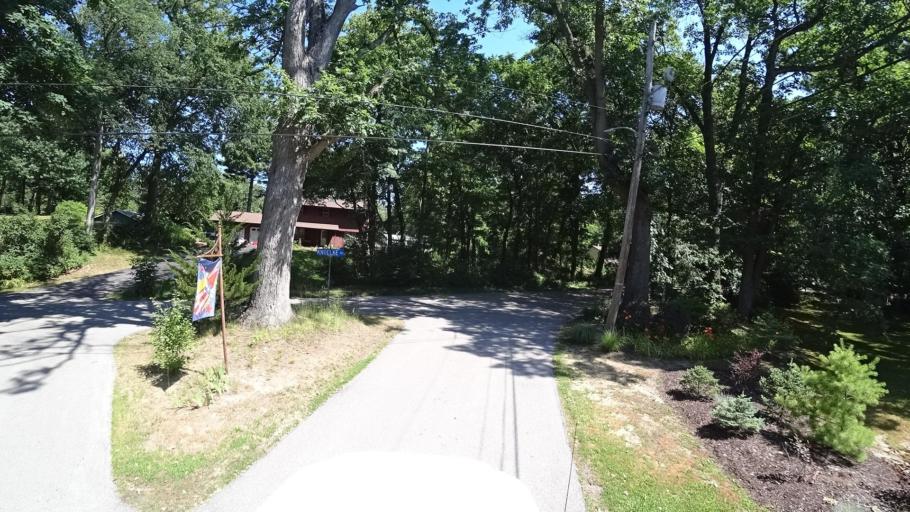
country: US
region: Indiana
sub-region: Porter County
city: Porter
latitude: 41.6376
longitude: -87.0709
